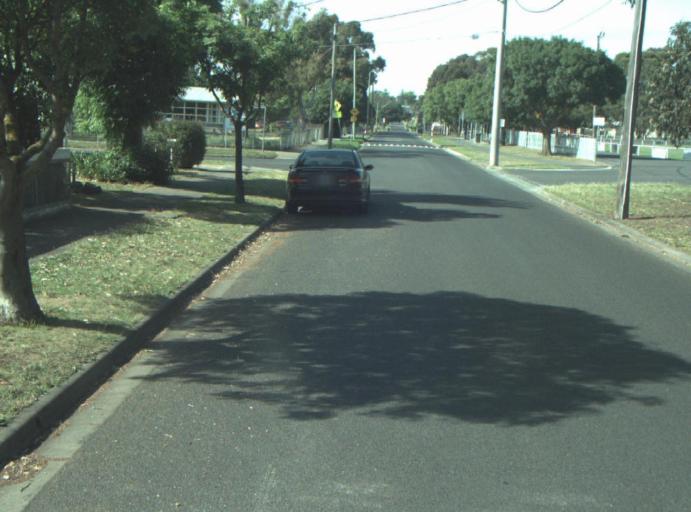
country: AU
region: Victoria
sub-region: Greater Geelong
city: Hamlyn Heights
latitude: -38.1239
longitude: 144.3325
